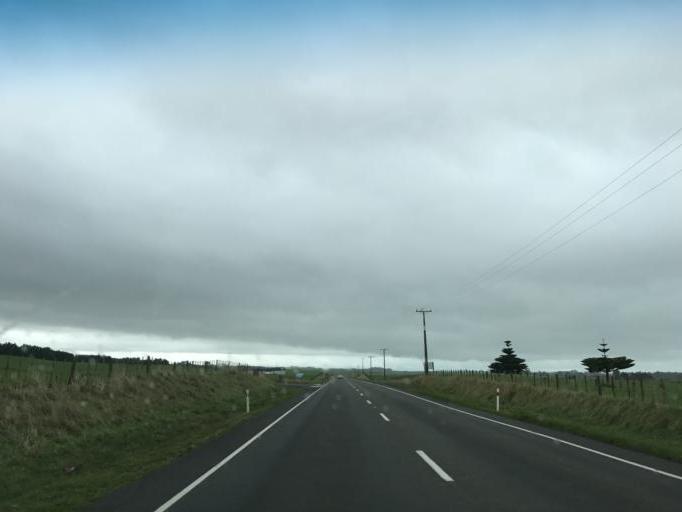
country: NZ
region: Manawatu-Wanganui
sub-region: Wanganui District
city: Wanganui
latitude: -39.8149
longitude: 174.8135
